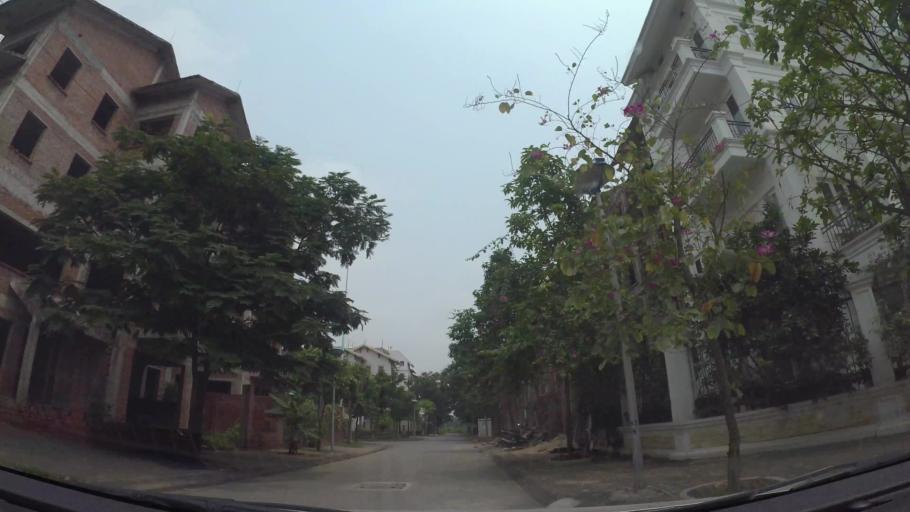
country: VN
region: Ha Noi
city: Cau Dien
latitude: 21.0244
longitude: 105.7444
